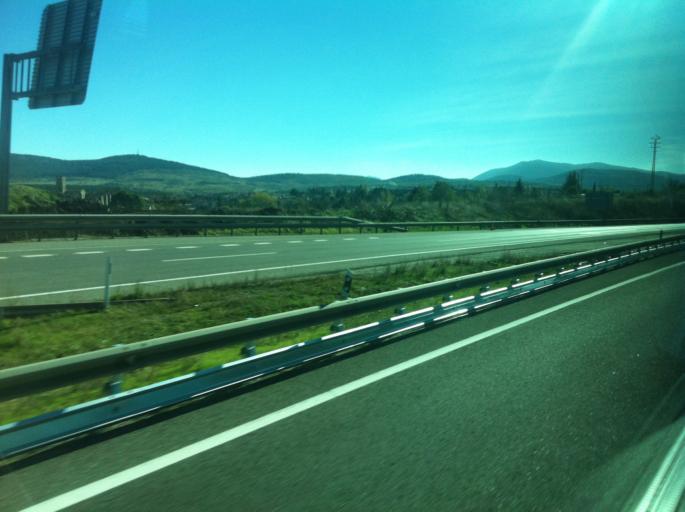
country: ES
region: Madrid
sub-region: Provincia de Madrid
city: Buitrago del Lozoya
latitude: 41.0008
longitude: -3.6384
